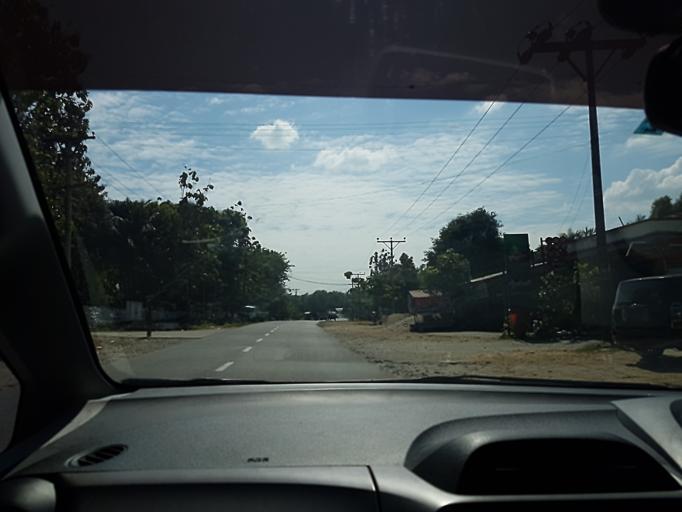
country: MM
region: Mon
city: Thaton
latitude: 16.7094
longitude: 97.4218
